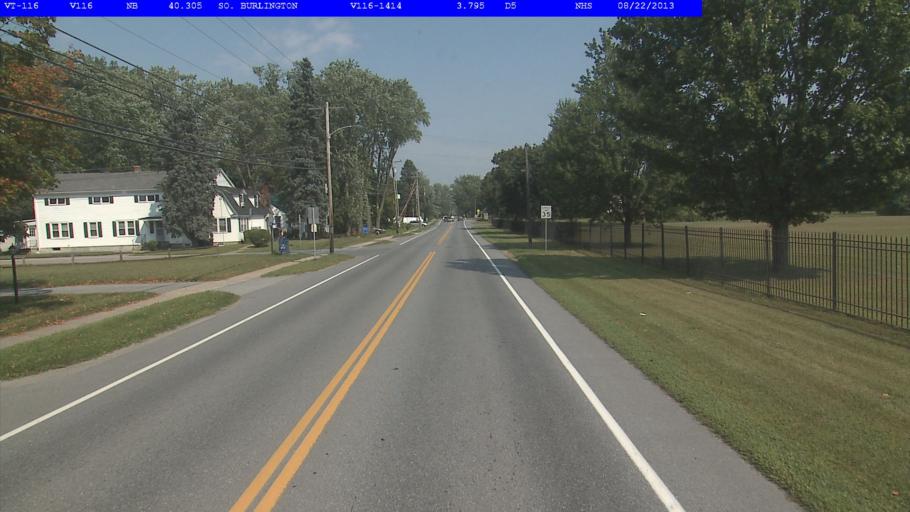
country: US
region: Vermont
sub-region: Chittenden County
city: South Burlington
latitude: 44.4606
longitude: -73.1701
